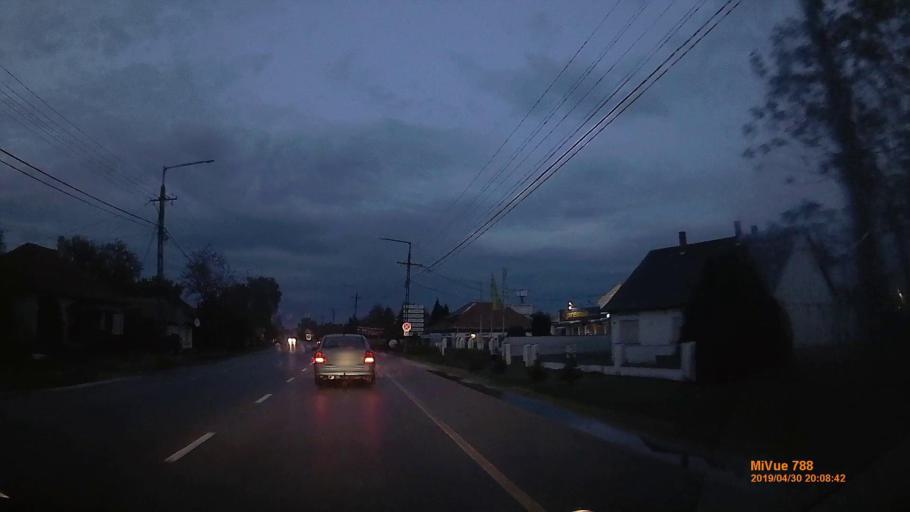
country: HU
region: Pest
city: Abony
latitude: 47.1841
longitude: 20.0448
